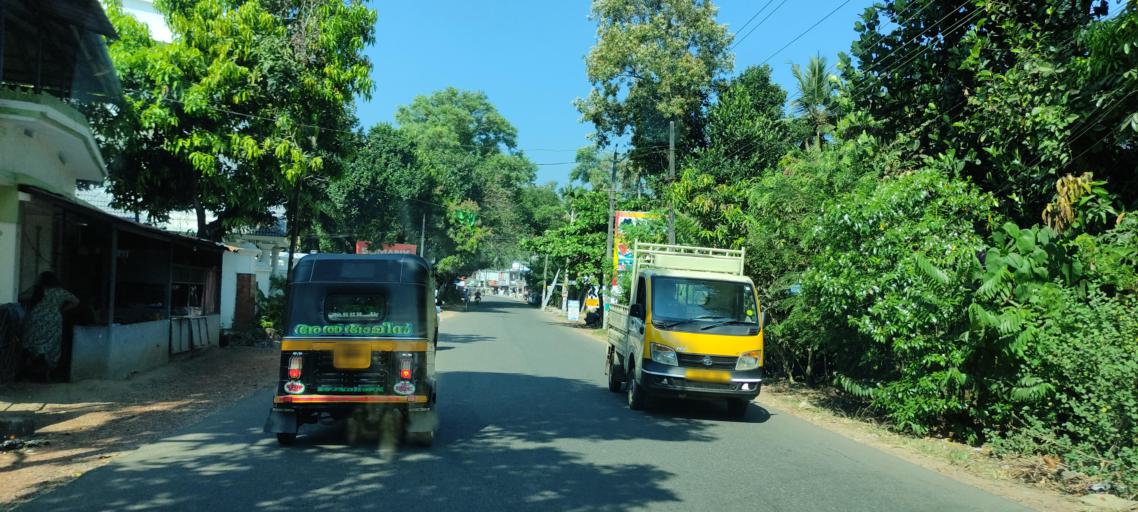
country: IN
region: Kerala
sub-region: Kollam
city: Panmana
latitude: 9.0517
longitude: 76.5626
